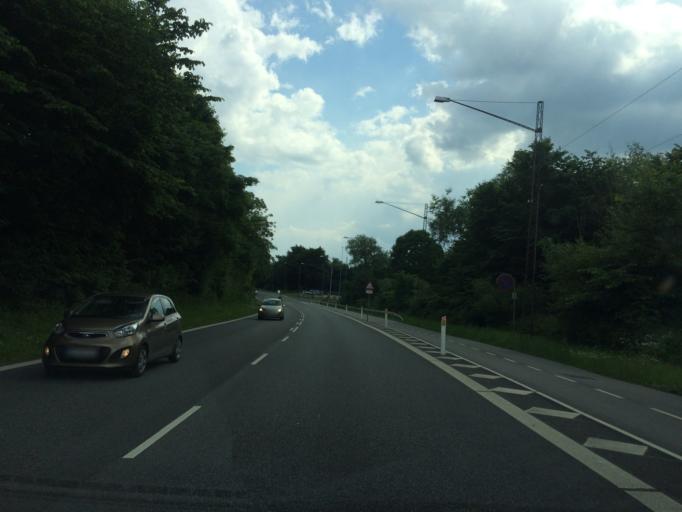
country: DK
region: South Denmark
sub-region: Fredericia Kommune
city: Snoghoj
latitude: 55.5113
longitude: 9.7028
